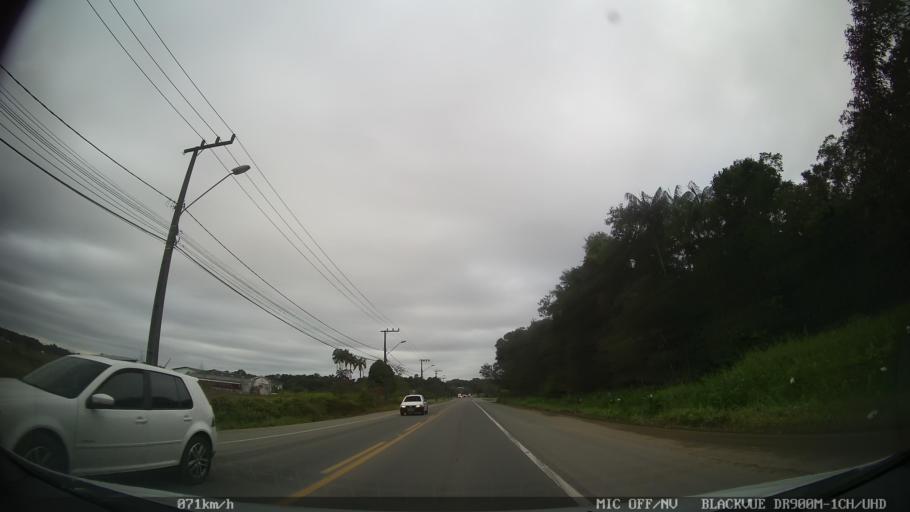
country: BR
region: Santa Catarina
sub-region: Joinville
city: Joinville
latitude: -26.2757
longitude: -48.9238
